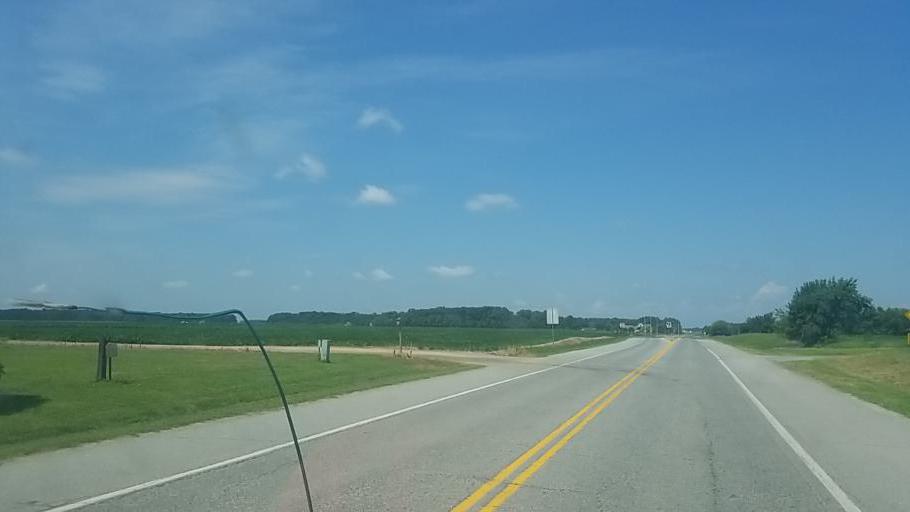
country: US
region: Maryland
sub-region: Caroline County
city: Denton
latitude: 38.8931
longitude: -75.8472
